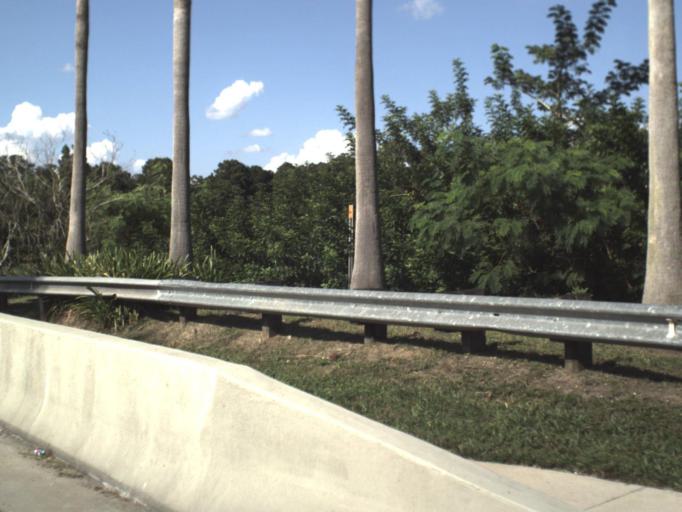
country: US
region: Florida
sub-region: Hillsborough County
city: Temple Terrace
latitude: 28.0238
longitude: -82.3934
